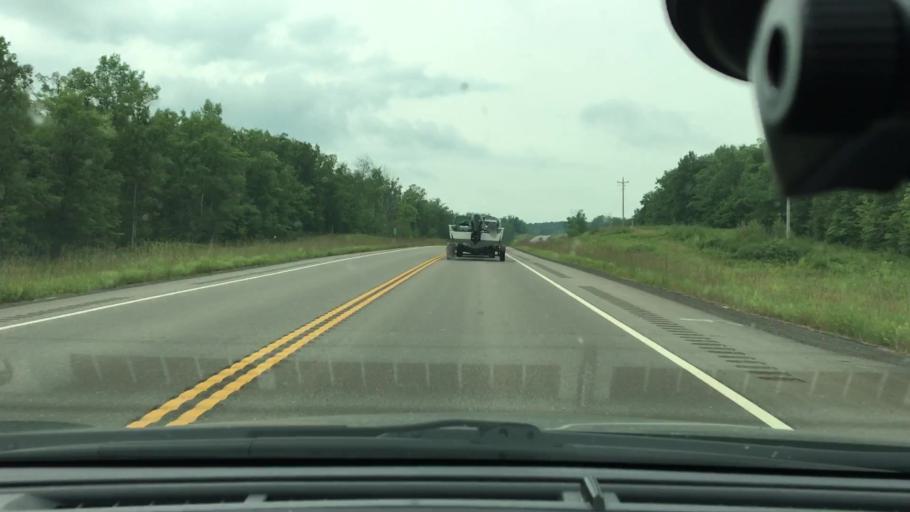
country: US
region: Minnesota
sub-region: Crow Wing County
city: Crosby
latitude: 46.6101
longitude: -93.9492
